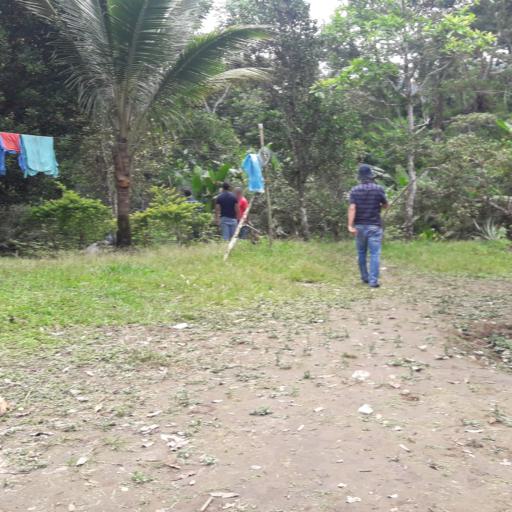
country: EC
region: Napo
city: Archidona
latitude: -0.9407
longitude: -77.8765
